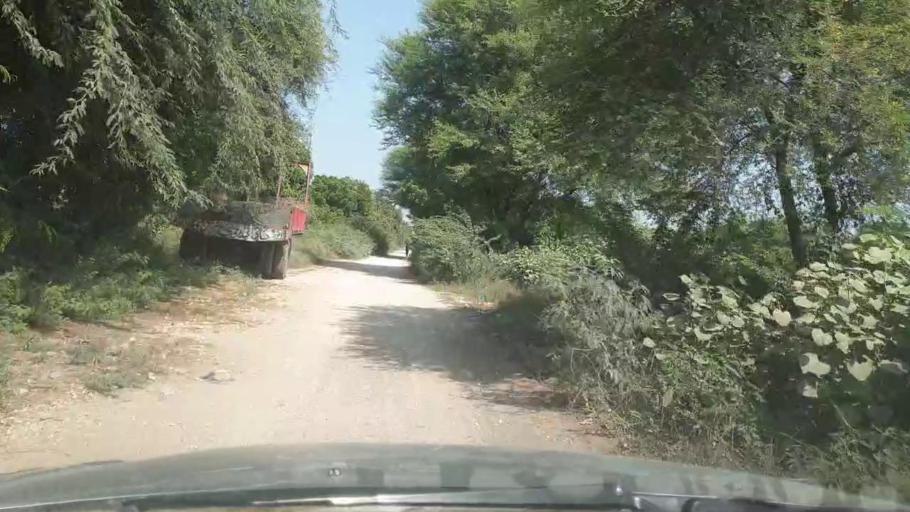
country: PK
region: Sindh
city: Tando Ghulam Ali
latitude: 25.1928
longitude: 68.8779
